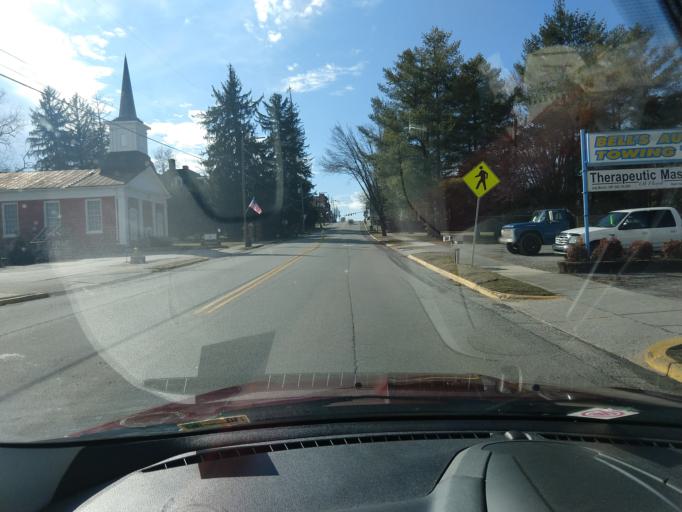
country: US
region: Virginia
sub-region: Floyd County
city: Floyd
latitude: 36.9117
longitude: -80.3174
